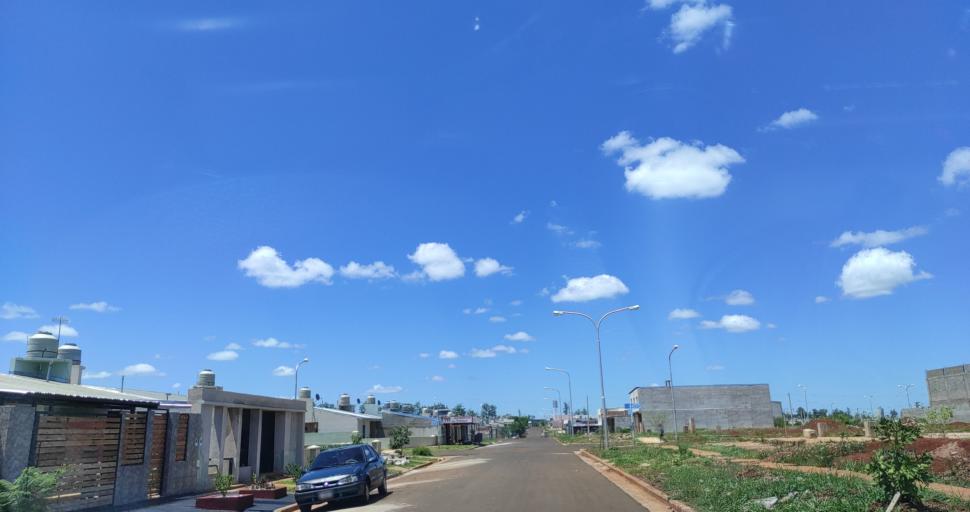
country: AR
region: Misiones
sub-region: Departamento de Capital
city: Posadas
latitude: -27.4064
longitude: -55.9826
